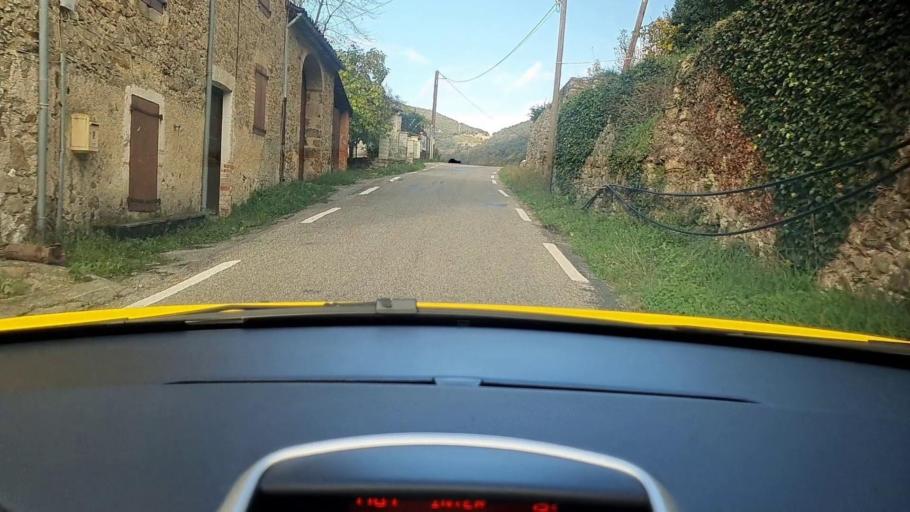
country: FR
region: Languedoc-Roussillon
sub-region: Departement du Gard
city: Lasalle
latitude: 44.0679
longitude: 3.8338
